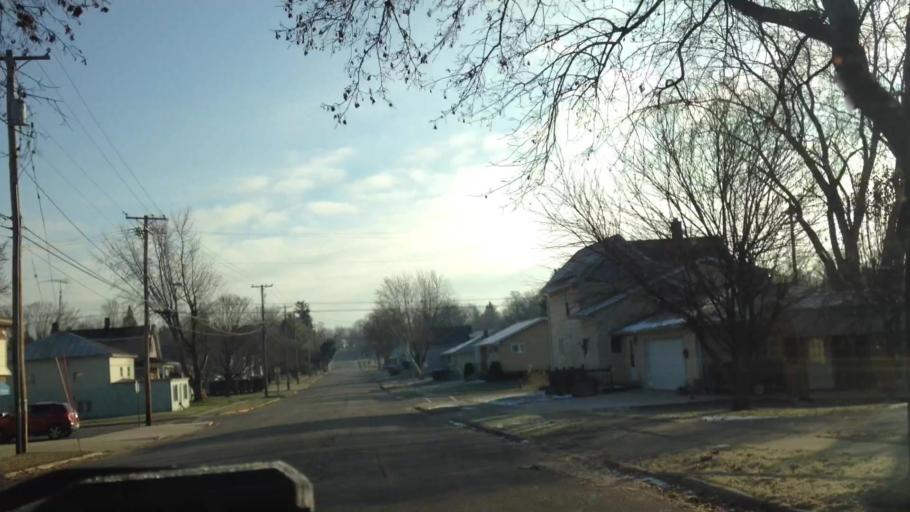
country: US
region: Wisconsin
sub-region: Dodge County
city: Mayville
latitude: 43.5012
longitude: -88.5522
